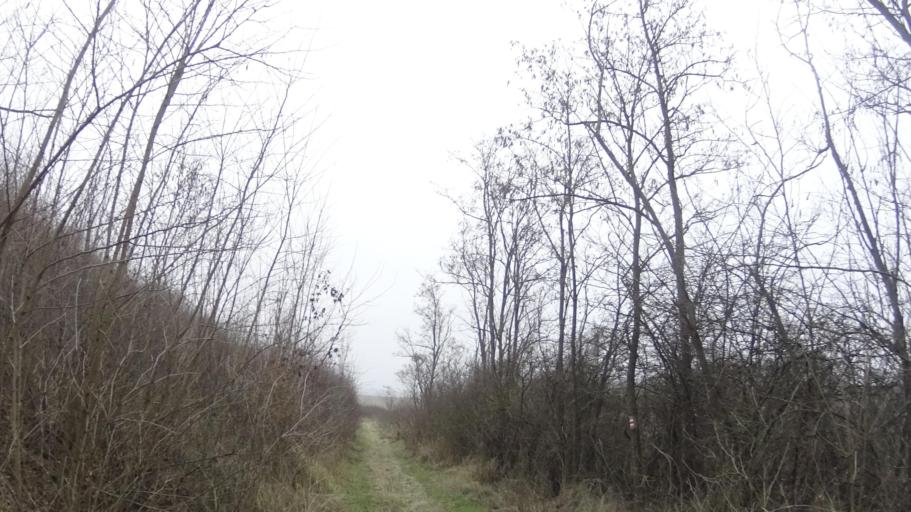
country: HU
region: Pest
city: Kosd
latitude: 47.7788
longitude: 19.2199
